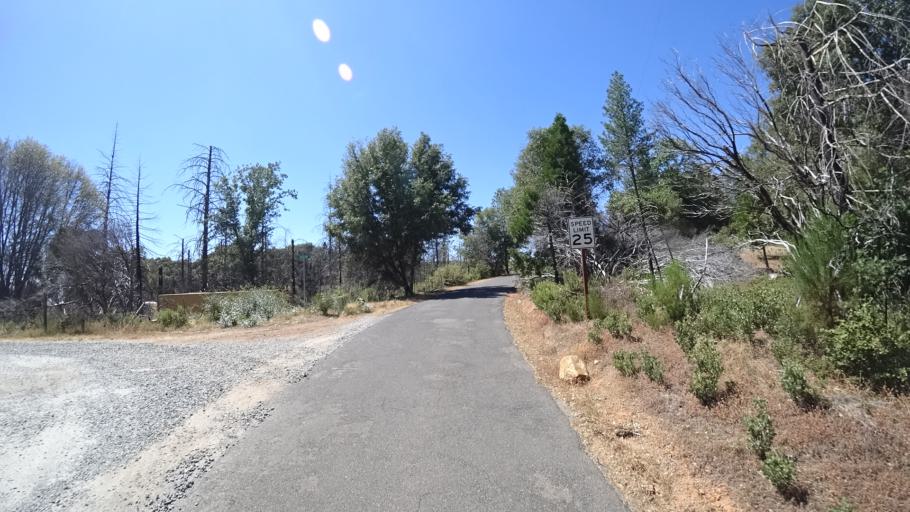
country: US
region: California
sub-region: Calaveras County
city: Mountain Ranch
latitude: 38.2765
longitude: -120.5499
